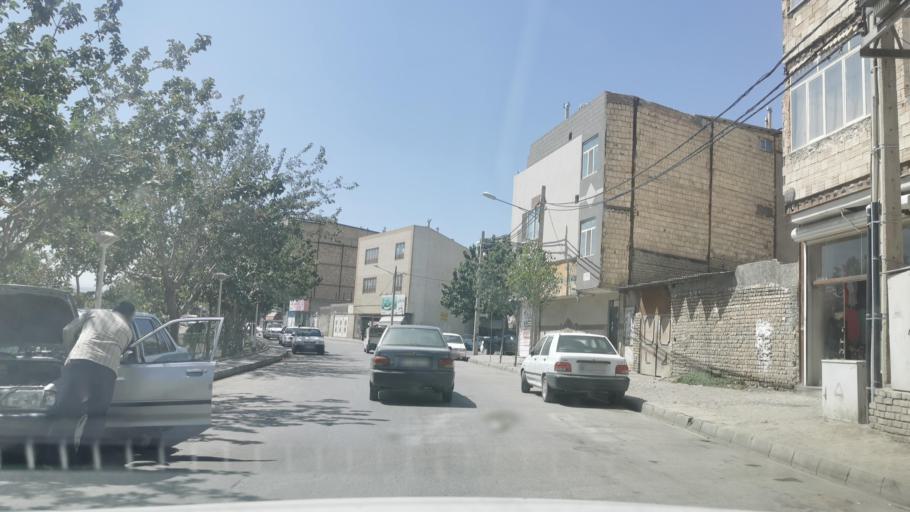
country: IR
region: Razavi Khorasan
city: Mashhad
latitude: 36.3612
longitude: 59.5546
